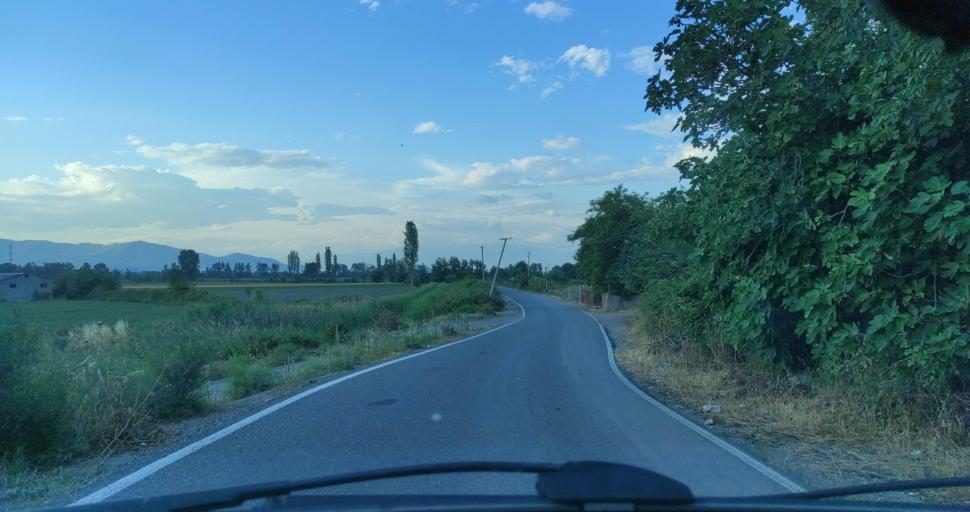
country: AL
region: Shkoder
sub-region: Rrethi i Shkodres
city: Velipoje
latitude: 41.9282
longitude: 19.4699
